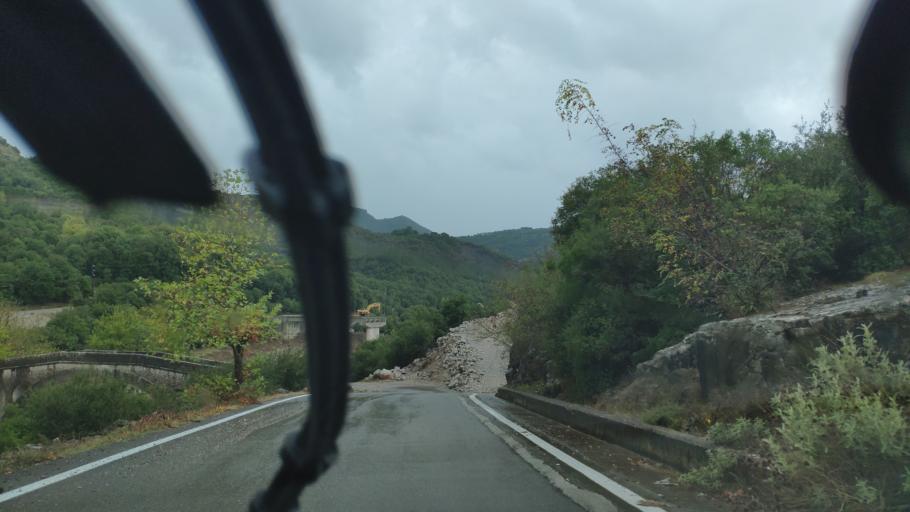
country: GR
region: Central Greece
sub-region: Nomos Evrytanias
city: Kerasochori
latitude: 39.1013
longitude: 21.4336
